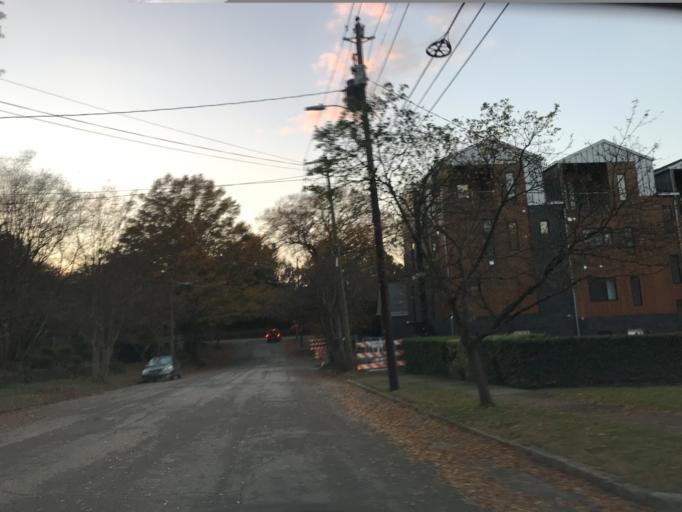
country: US
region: North Carolina
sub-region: Wake County
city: West Raleigh
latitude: 35.7829
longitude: -78.6495
